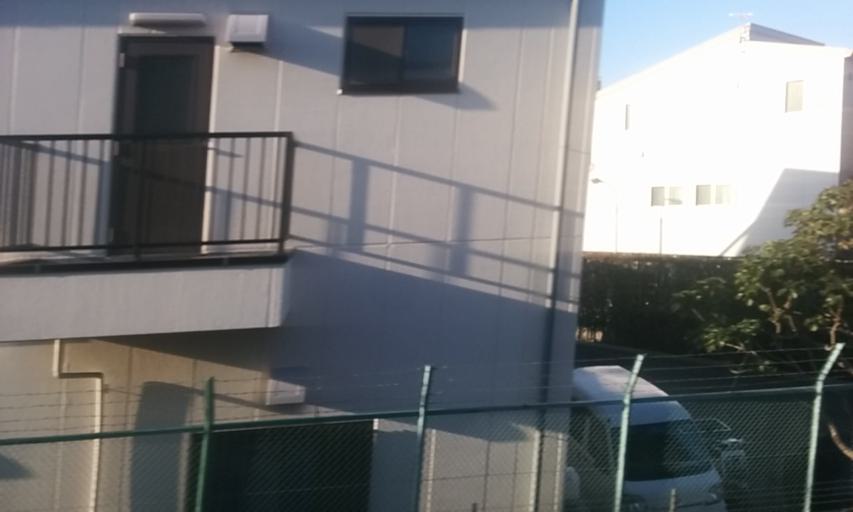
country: JP
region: Saitama
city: Kawaguchi
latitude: 35.7540
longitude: 139.6987
